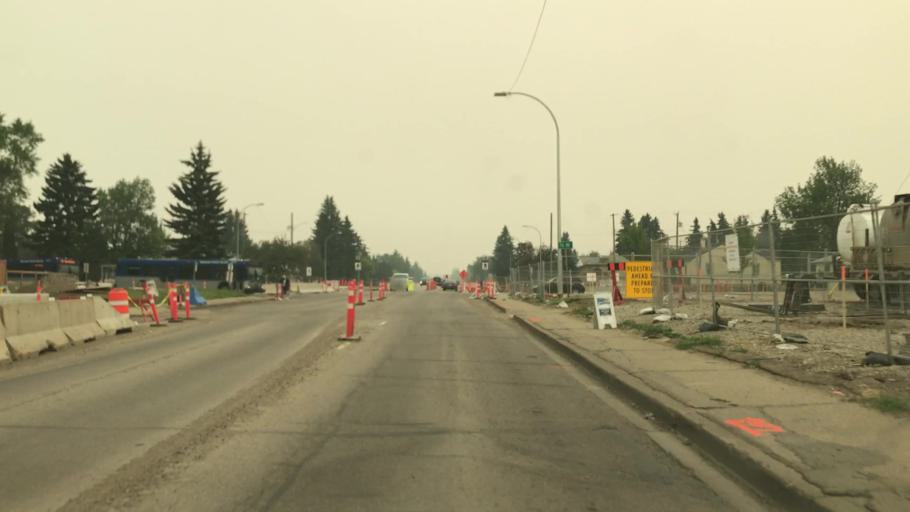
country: CA
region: Alberta
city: Edmonton
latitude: 53.5130
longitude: -113.4552
